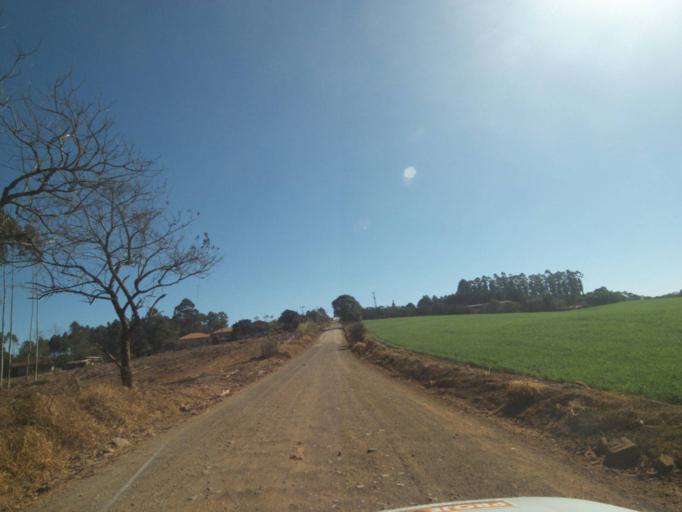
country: BR
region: Parana
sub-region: Reserva
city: Reserva
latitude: -24.6248
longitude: -50.6307
